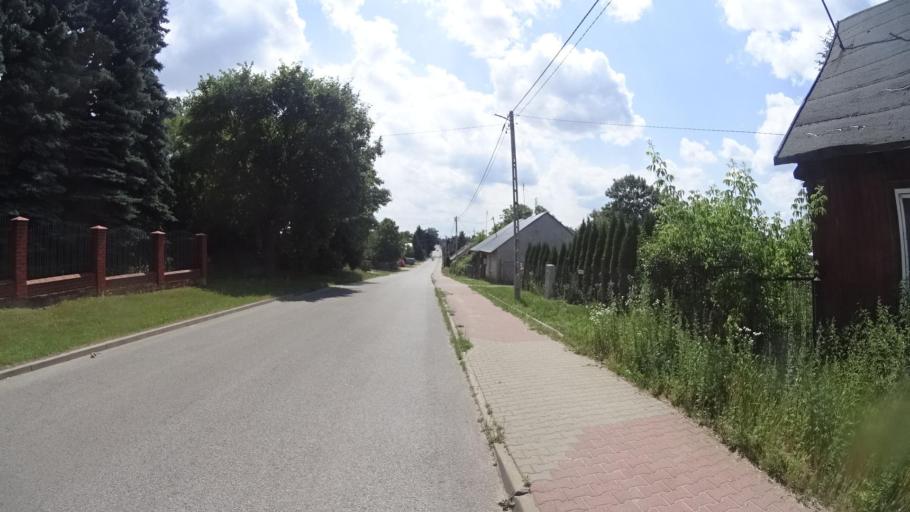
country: PL
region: Masovian Voivodeship
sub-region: Powiat grojecki
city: Goszczyn
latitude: 51.7296
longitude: 20.8517
